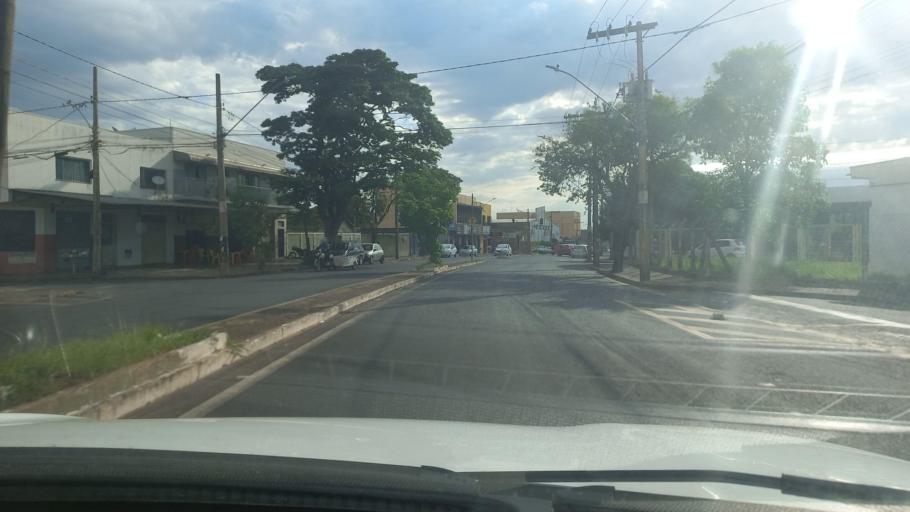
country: BR
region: Minas Gerais
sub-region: Uberaba
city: Uberaba
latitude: -19.7673
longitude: -47.9217
